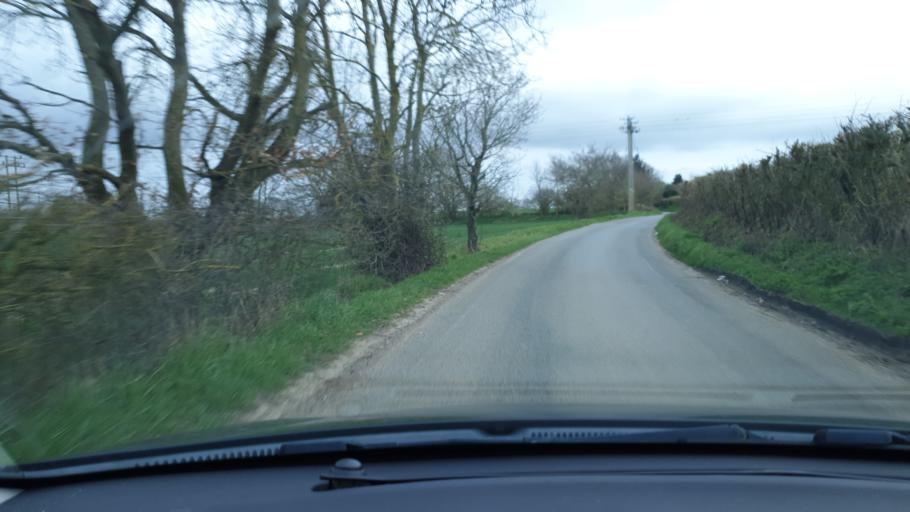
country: GB
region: England
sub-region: Suffolk
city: Shotley Gate
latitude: 51.9289
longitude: 1.1778
